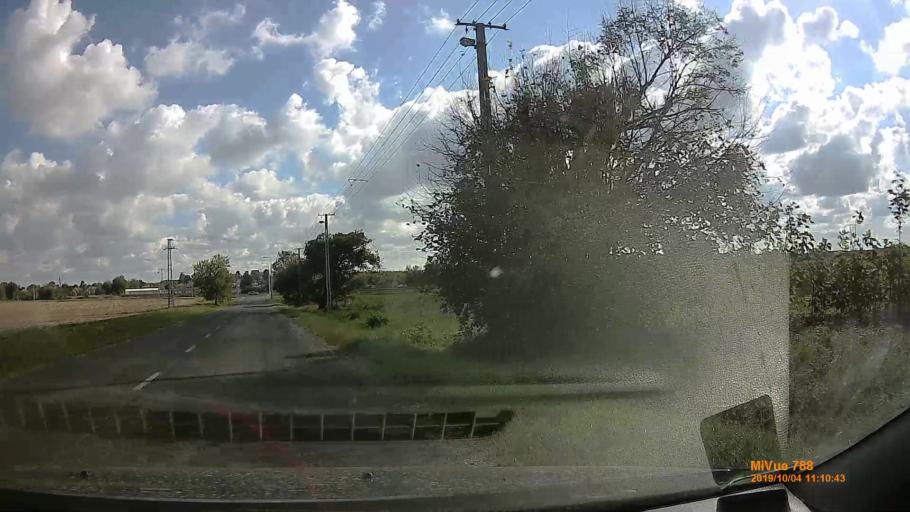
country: HU
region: Somogy
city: Kaposvar
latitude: 46.4138
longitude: 17.7689
